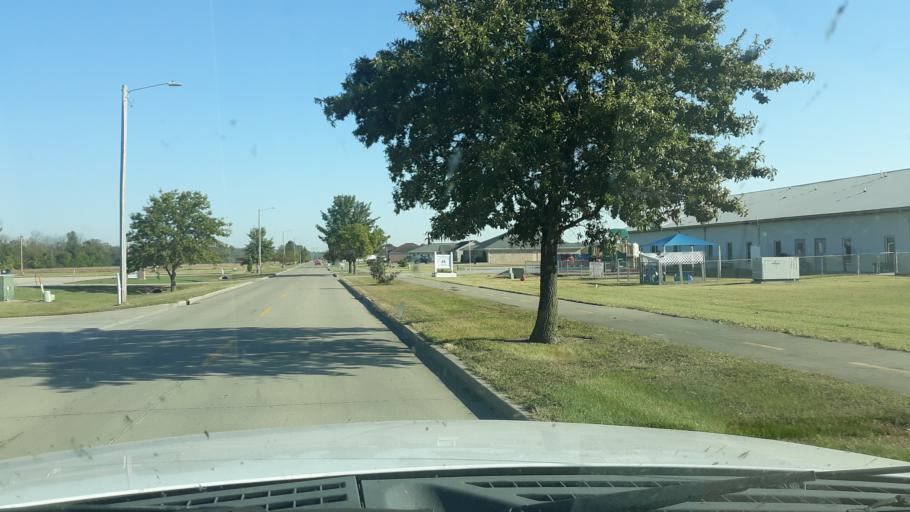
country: US
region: Illinois
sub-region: Saline County
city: Harrisburg
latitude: 37.7447
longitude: -88.5314
